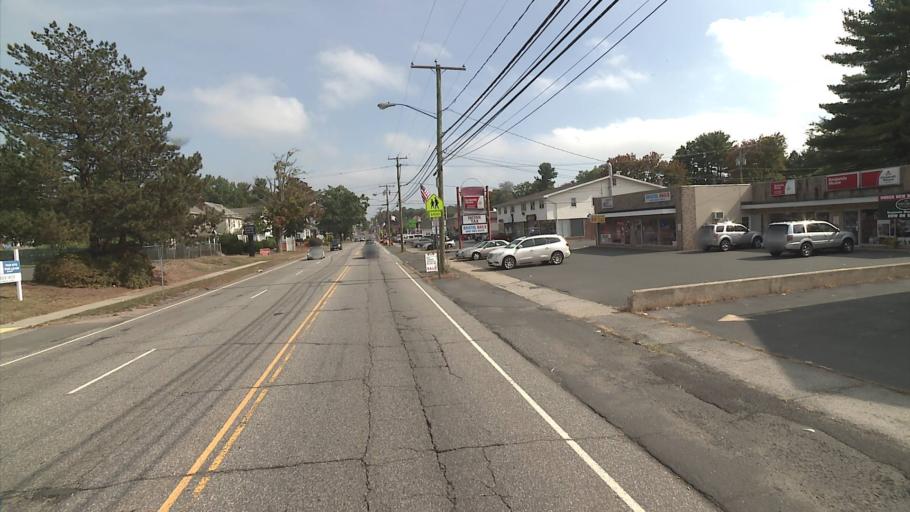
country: US
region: Connecticut
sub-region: Hartford County
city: Bristol
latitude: 41.6915
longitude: -72.9200
